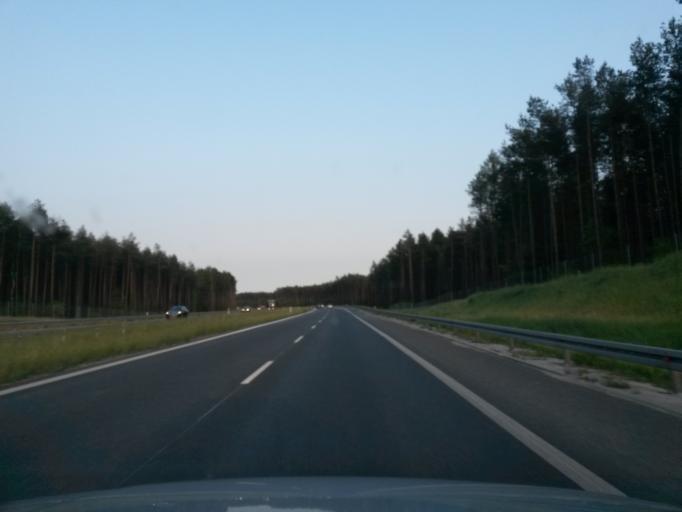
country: PL
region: Greater Poland Voivodeship
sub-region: Powiat kepinski
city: Perzow
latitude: 51.2989
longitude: 17.8077
